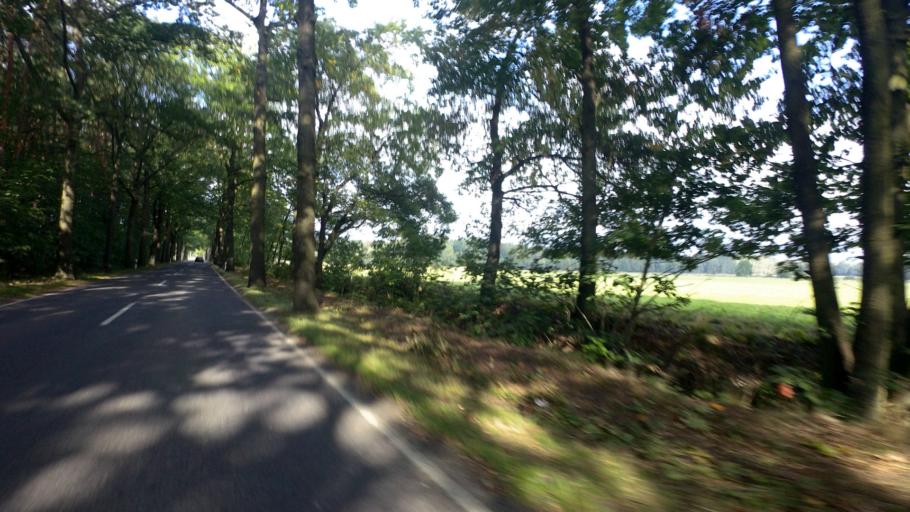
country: DE
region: Saxony
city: Wiednitz
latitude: 51.3851
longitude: 14.0479
